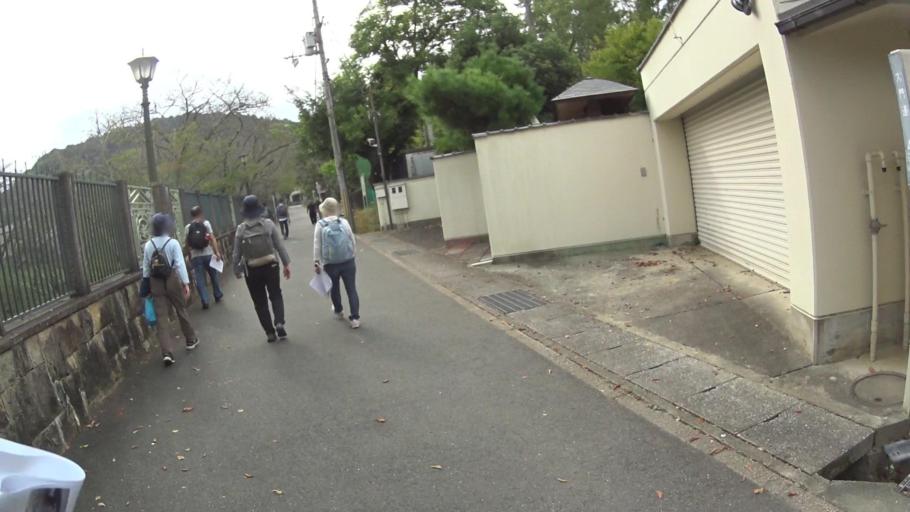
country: JP
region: Shiga Prefecture
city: Nagahama
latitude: 35.3945
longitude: 136.2335
